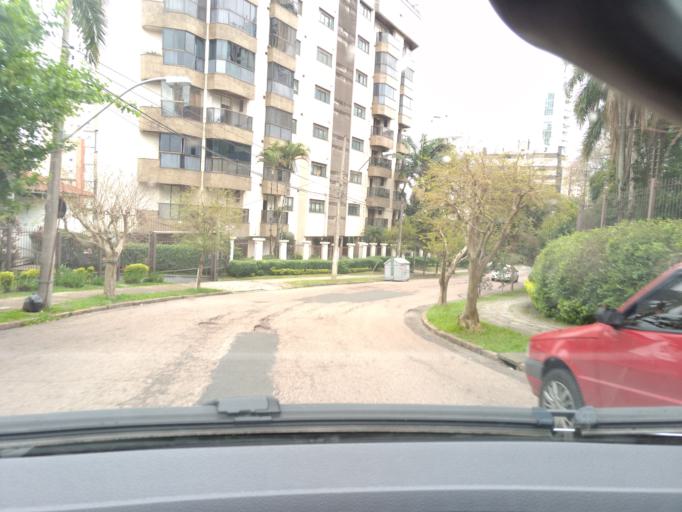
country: BR
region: Rio Grande do Sul
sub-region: Porto Alegre
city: Porto Alegre
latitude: -30.0325
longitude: -51.1806
